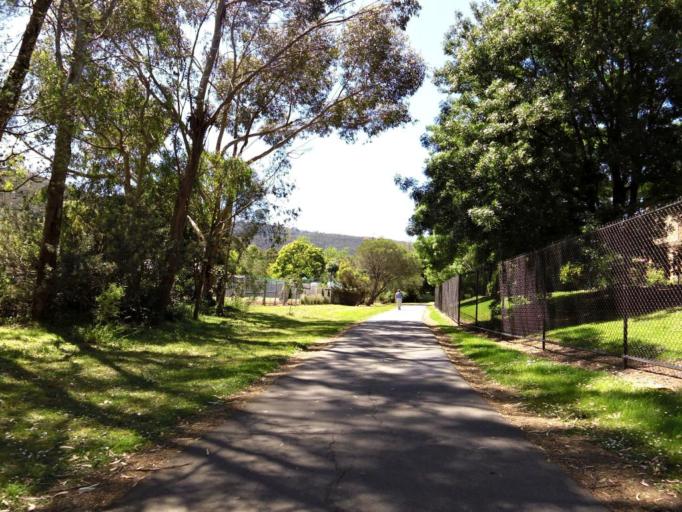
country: AU
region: Victoria
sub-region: Knox
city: Ferntree Gully
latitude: -37.8951
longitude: 145.3045
